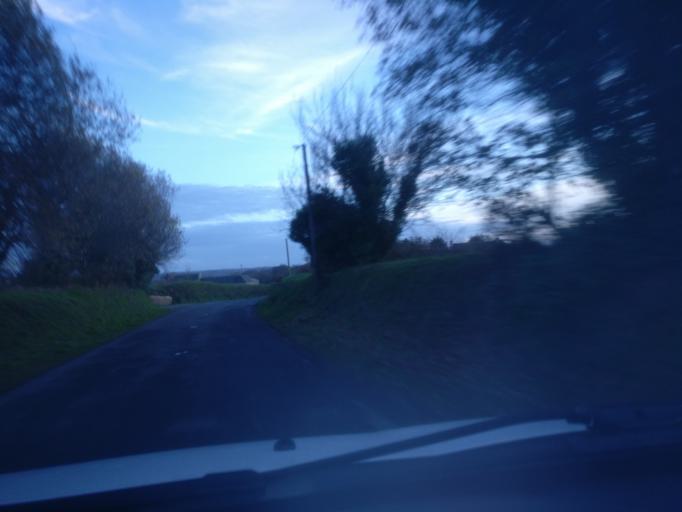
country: FR
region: Brittany
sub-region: Departement des Cotes-d'Armor
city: Saint-Quay-Perros
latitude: 48.8015
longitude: -3.4621
